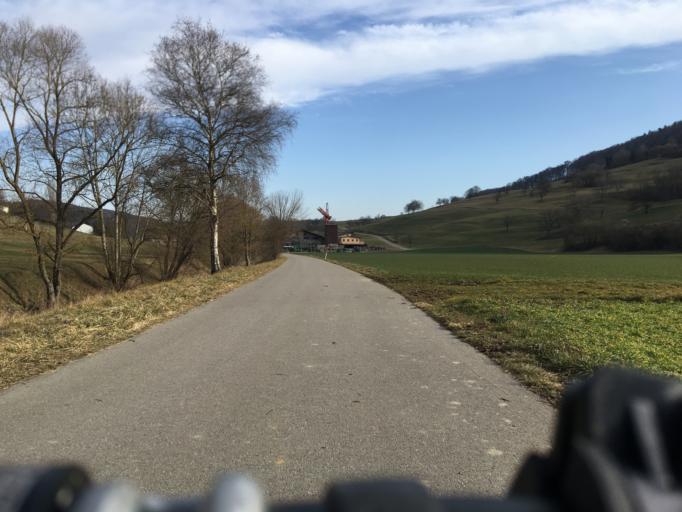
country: CH
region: Schaffhausen
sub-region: Bezirk Reiat
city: Stetten
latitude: 47.7756
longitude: 8.6698
